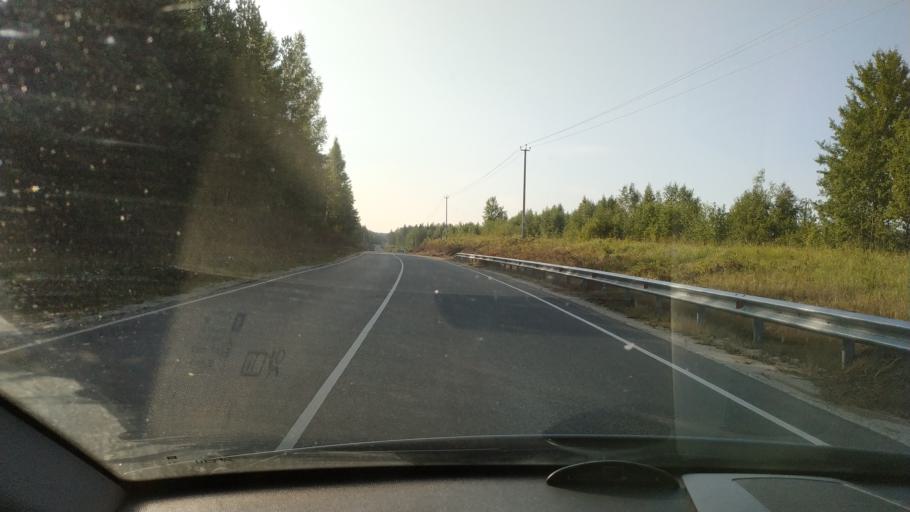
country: RU
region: Moskovskaya
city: Tugolesskiy Bor
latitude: 55.4316
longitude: 39.7236
